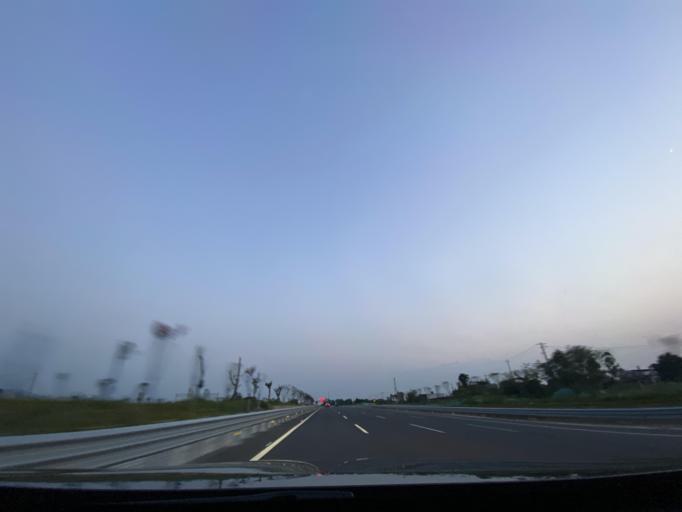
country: CN
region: Sichuan
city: Longquan
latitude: 30.4994
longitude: 104.1931
